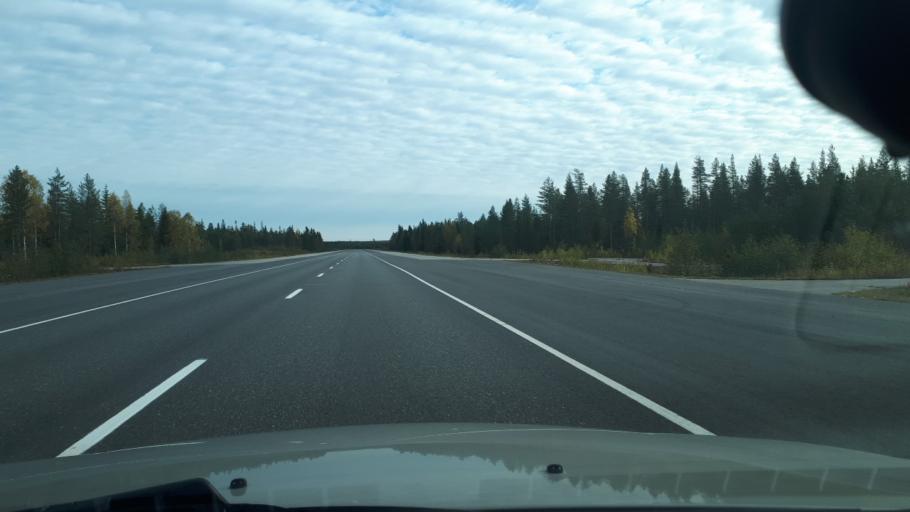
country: FI
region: Northern Ostrobothnia
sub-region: Oulu
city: Yli-Ii
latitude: 65.8958
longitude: 25.7022
